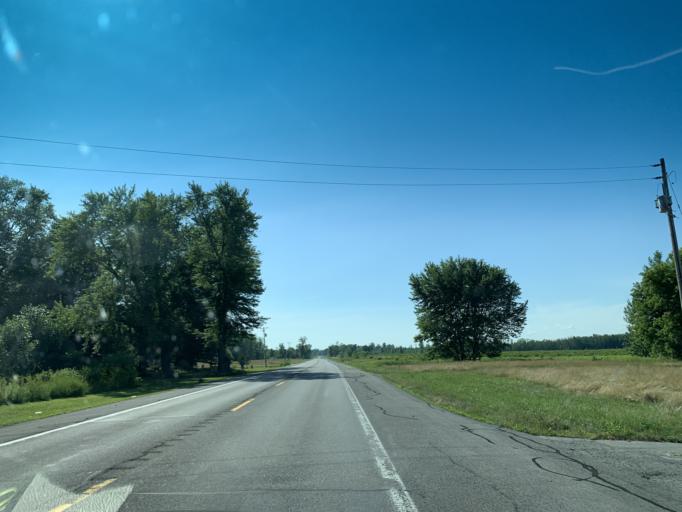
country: US
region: New York
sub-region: Madison County
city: Oneida
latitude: 43.1408
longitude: -75.6314
